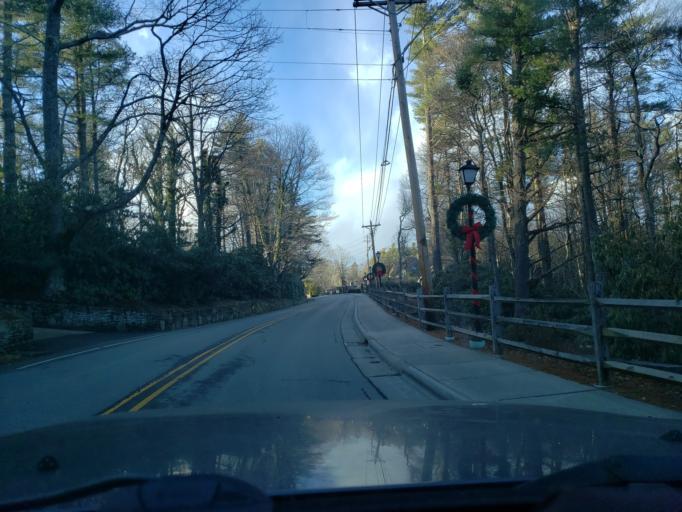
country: US
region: North Carolina
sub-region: Watauga County
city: Blowing Rock
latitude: 36.1233
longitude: -81.6753
